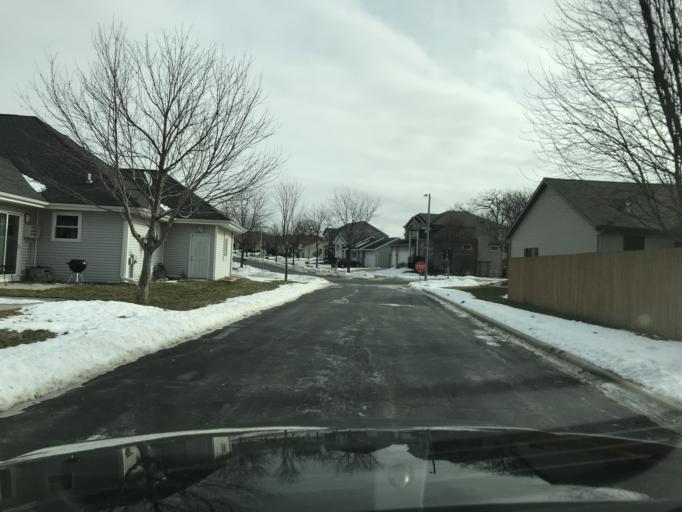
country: US
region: Wisconsin
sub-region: Dane County
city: Cottage Grove
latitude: 43.0928
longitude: -89.2618
